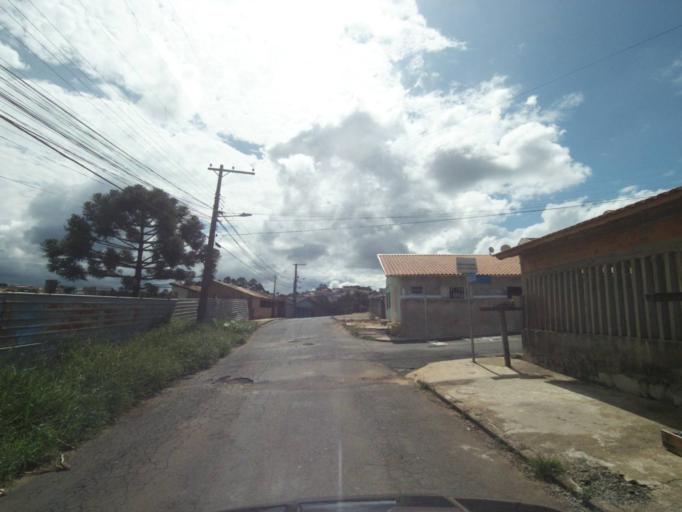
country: BR
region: Parana
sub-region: Telemaco Borba
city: Telemaco Borba
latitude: -24.3188
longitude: -50.6263
